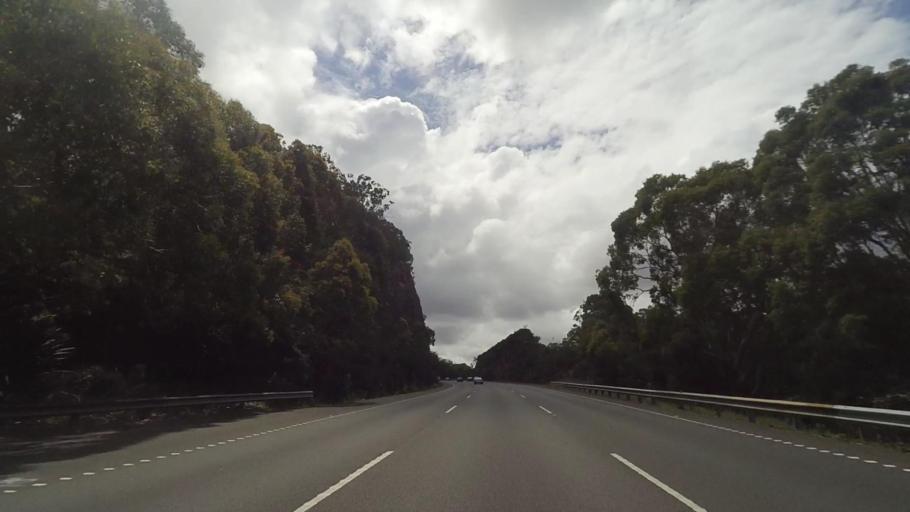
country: AU
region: New South Wales
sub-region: Hornsby Shire
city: Berowra Heights
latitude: -33.5207
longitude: 151.1964
